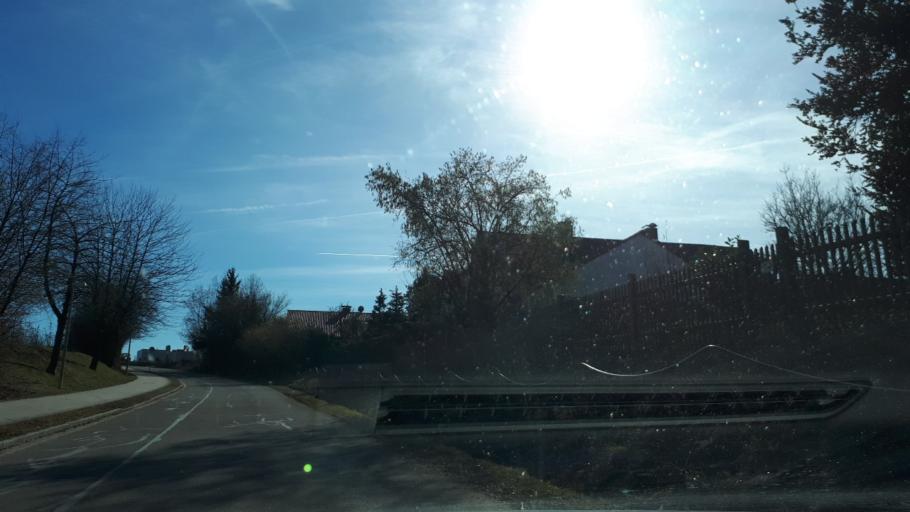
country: DE
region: Bavaria
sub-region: Upper Palatinate
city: Pentling
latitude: 48.9796
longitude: 12.0579
